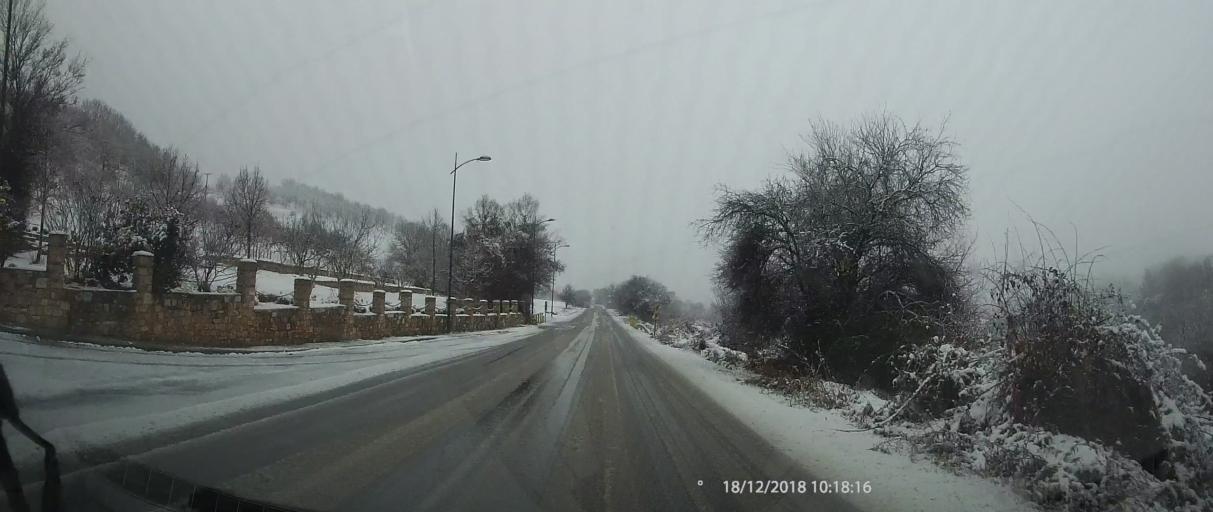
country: GR
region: Thessaly
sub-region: Nomos Larisis
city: Livadi
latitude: 40.1302
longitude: 22.2161
